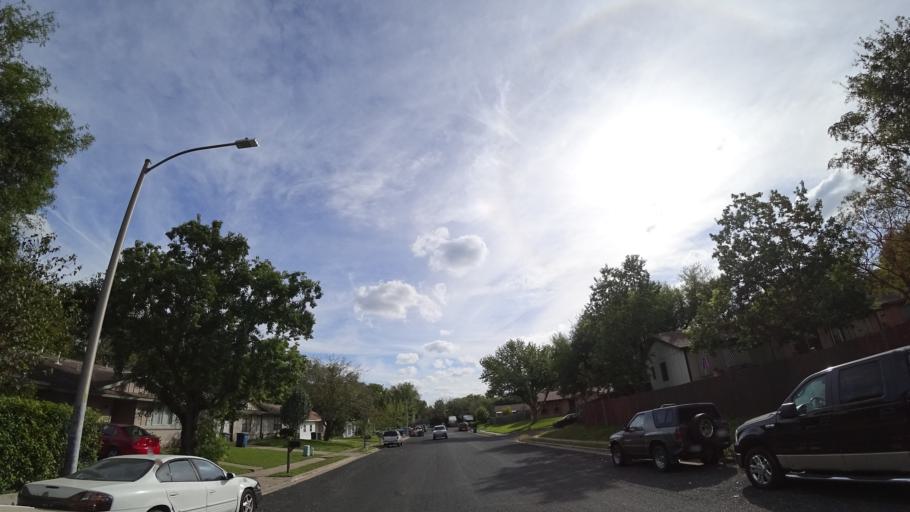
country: US
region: Texas
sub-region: Travis County
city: Austin
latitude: 30.2015
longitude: -97.7526
